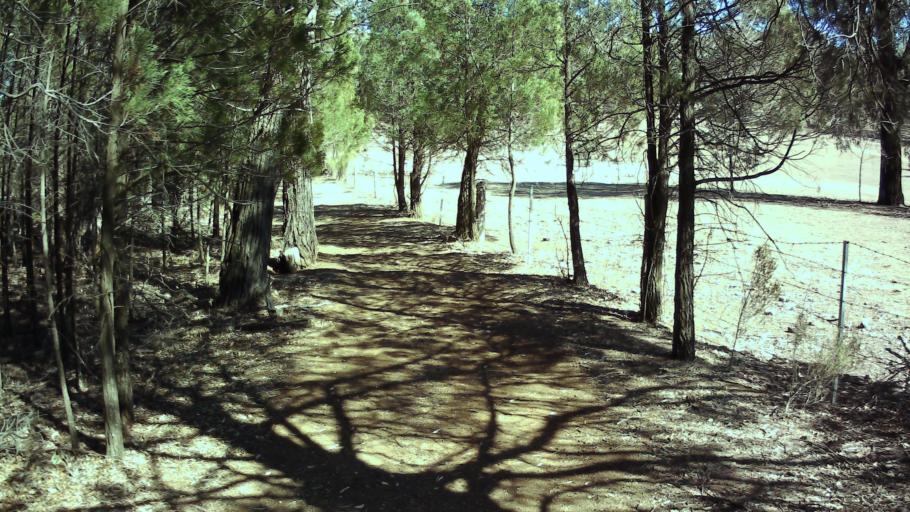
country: AU
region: New South Wales
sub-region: Weddin
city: Grenfell
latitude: -33.7401
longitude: 148.3665
